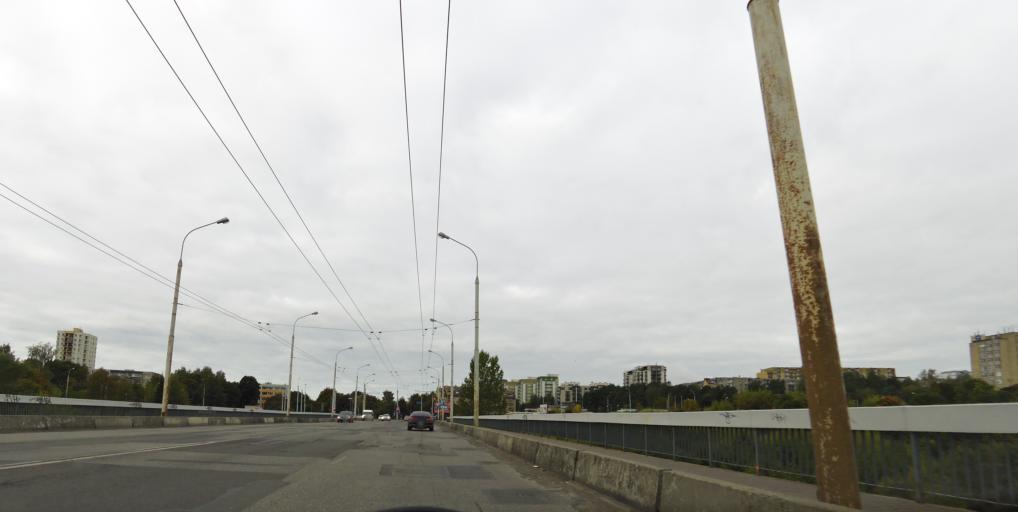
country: LT
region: Vilnius County
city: Rasos
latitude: 54.7055
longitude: 25.3074
